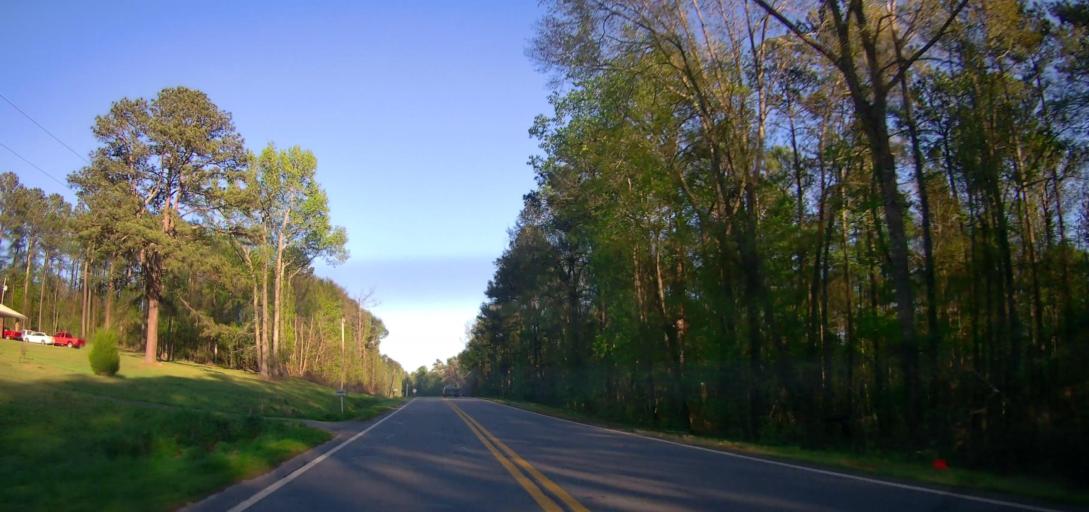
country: US
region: Georgia
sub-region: Wilkinson County
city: Irwinton
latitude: 32.8095
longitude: -83.1363
